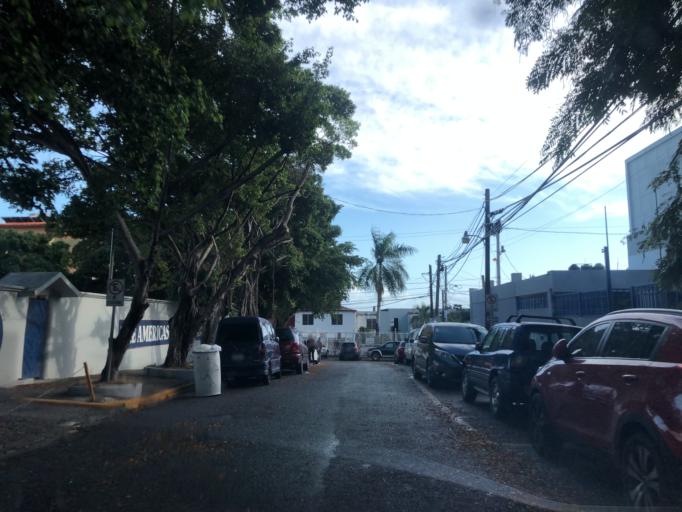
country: DO
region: Nacional
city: La Julia
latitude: 18.4587
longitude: -69.9286
